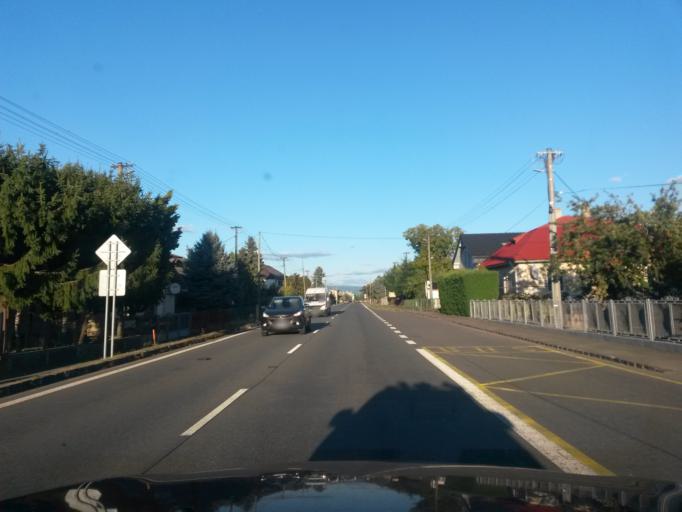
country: SK
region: Kosicky
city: Vinne
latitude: 48.7613
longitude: 21.9941
